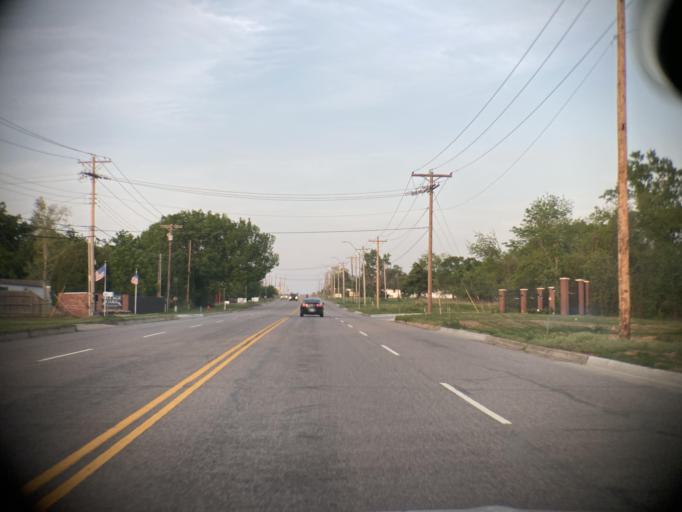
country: US
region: Oklahoma
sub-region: Oklahoma County
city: Midwest City
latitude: 35.4352
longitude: -97.3635
